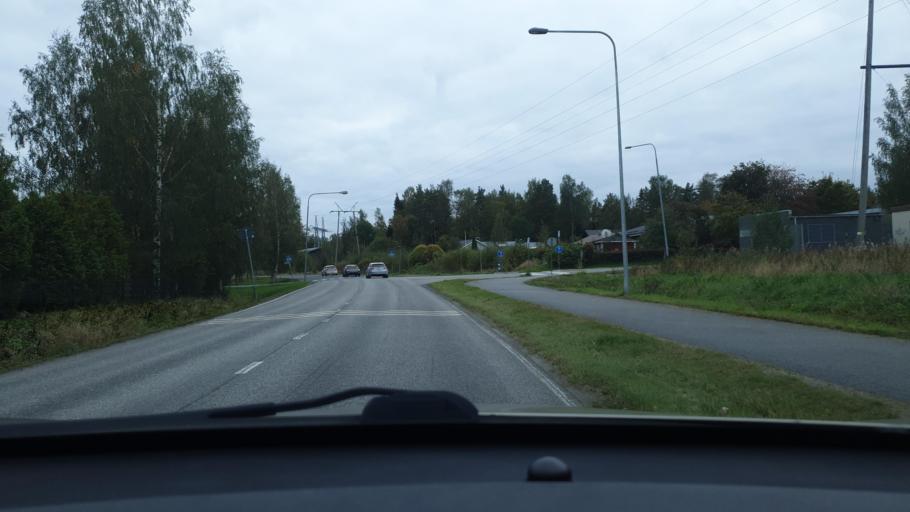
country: FI
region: Ostrobothnia
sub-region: Vaasa
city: Teeriniemi
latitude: 63.0951
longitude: 21.6977
